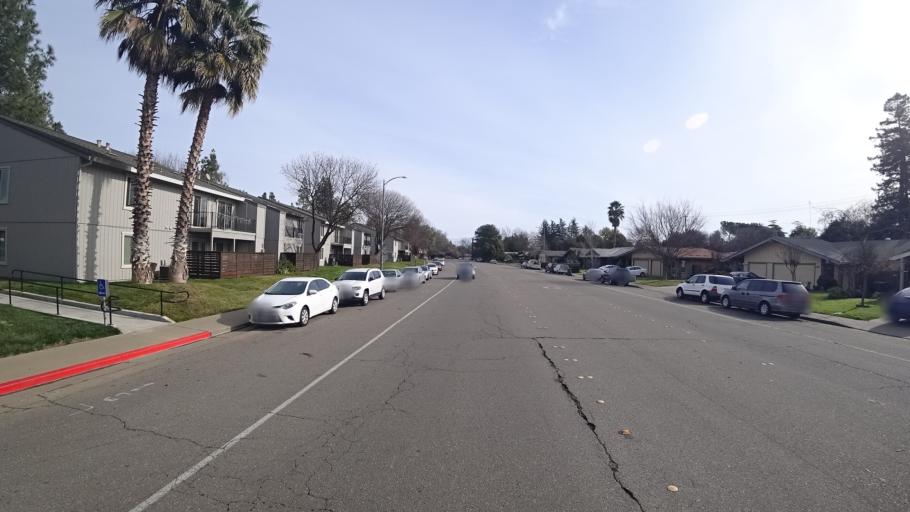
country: US
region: California
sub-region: Yolo County
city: Davis
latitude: 38.5488
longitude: -121.6933
